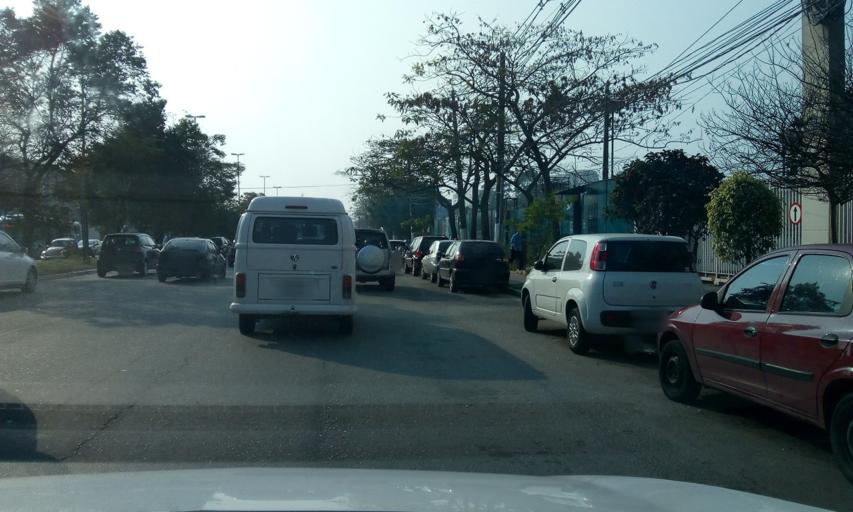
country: BR
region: Sao Paulo
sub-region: Diadema
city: Diadema
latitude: -23.6874
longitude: -46.6891
